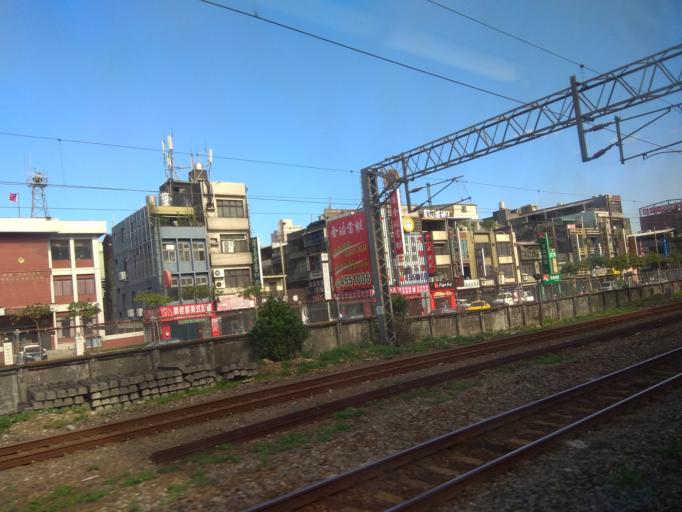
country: TW
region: Taiwan
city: Taoyuan City
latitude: 24.9717
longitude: 121.2559
